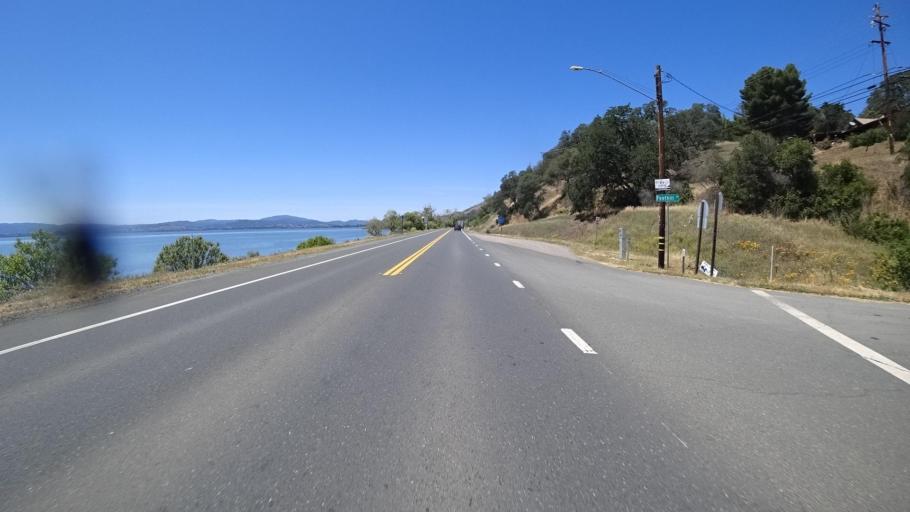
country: US
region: California
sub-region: Lake County
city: Lucerne
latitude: 39.0990
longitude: -122.8042
